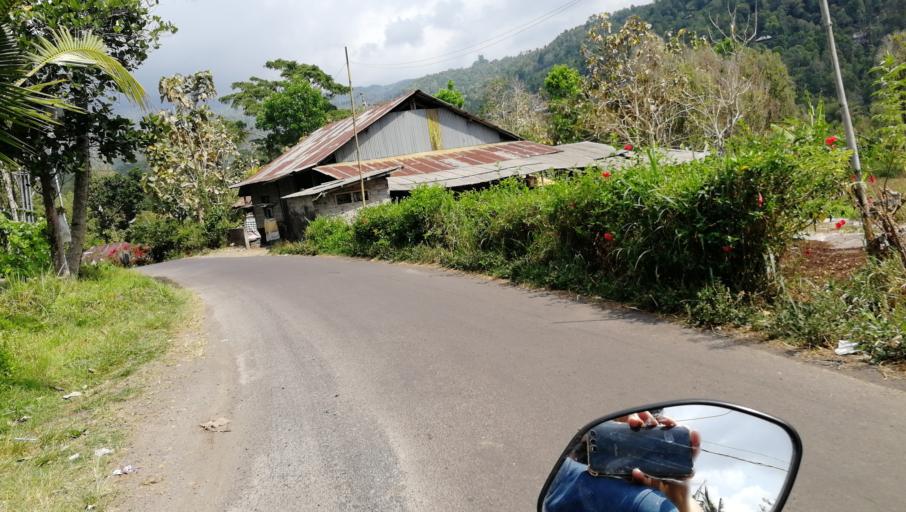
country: ID
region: Bali
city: Munduk
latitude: -8.2686
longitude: 115.0469
